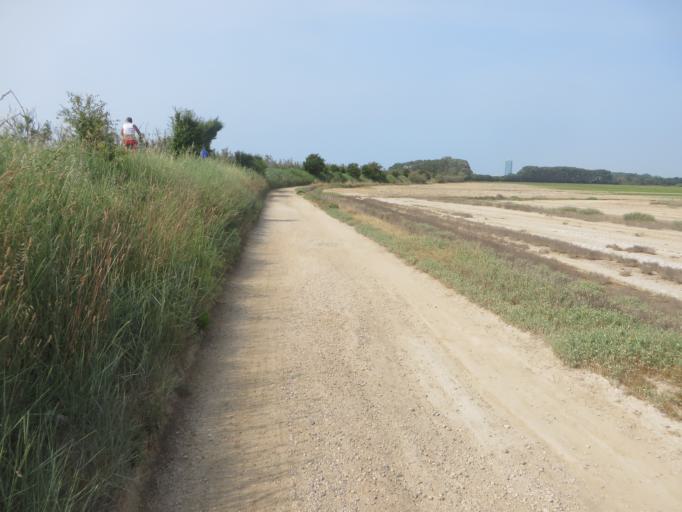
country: IT
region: Veneto
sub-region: Provincia di Venezia
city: Crepaldo
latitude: 45.5368
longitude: 12.7382
